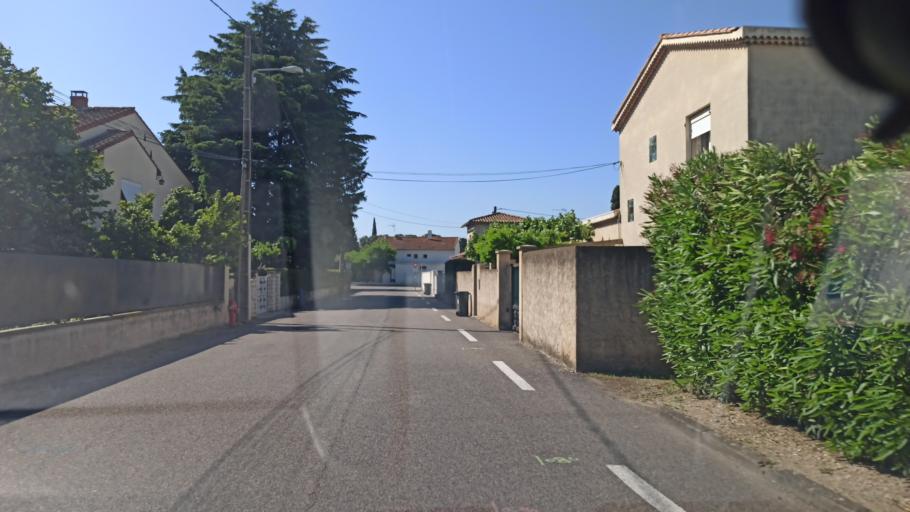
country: FR
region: Languedoc-Roussillon
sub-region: Departement du Gard
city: Les Angles
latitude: 43.9572
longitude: 4.7630
